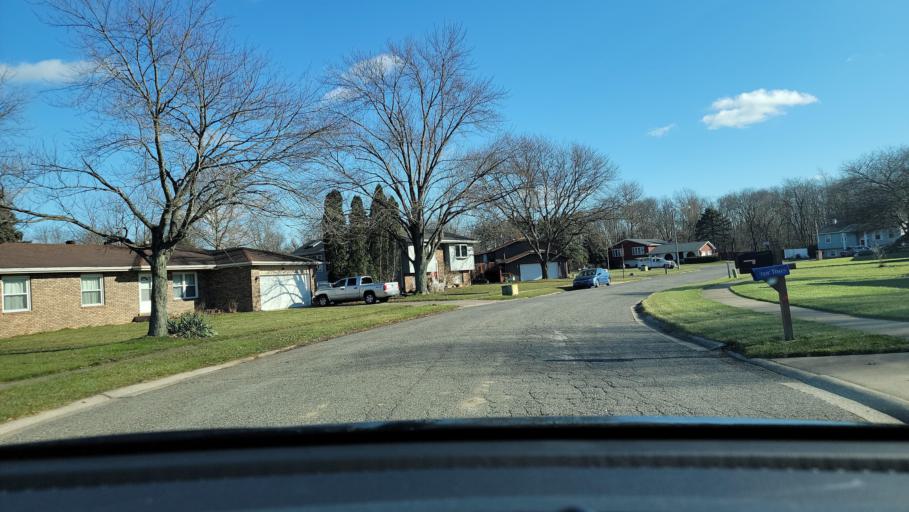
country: US
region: Indiana
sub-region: Porter County
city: Portage
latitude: 41.5628
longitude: -87.1887
